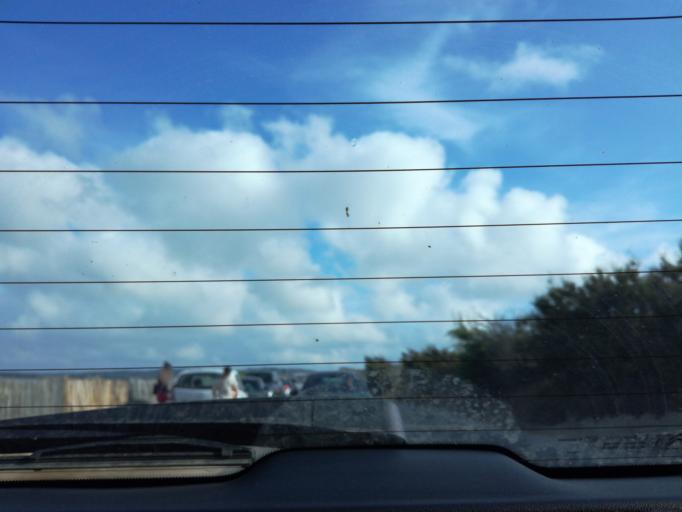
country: FR
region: Provence-Alpes-Cote d'Azur
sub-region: Departement du Var
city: Hyeres
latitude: 43.0643
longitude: 6.1313
